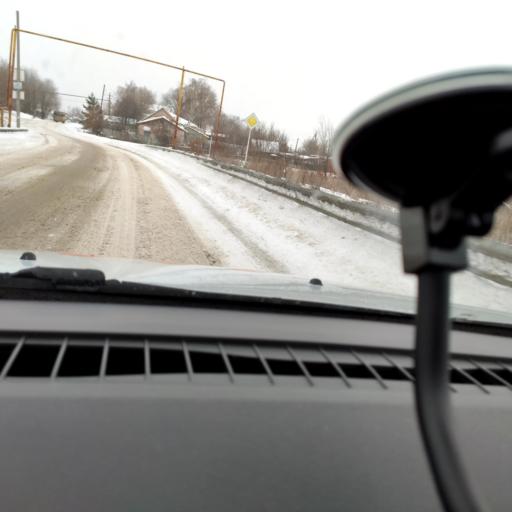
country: RU
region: Samara
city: Dubovyy Umet
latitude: 53.0397
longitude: 50.2426
